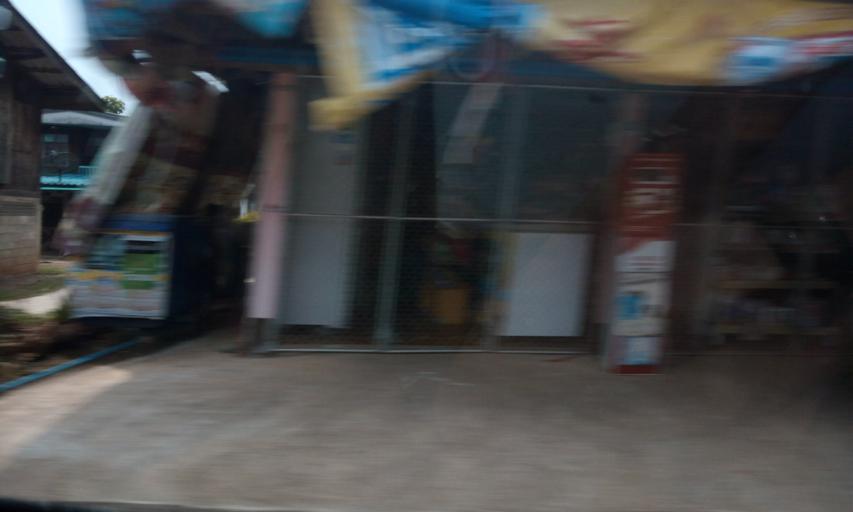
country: TH
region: Phayao
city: Phu Sang
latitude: 19.6106
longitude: 100.3220
